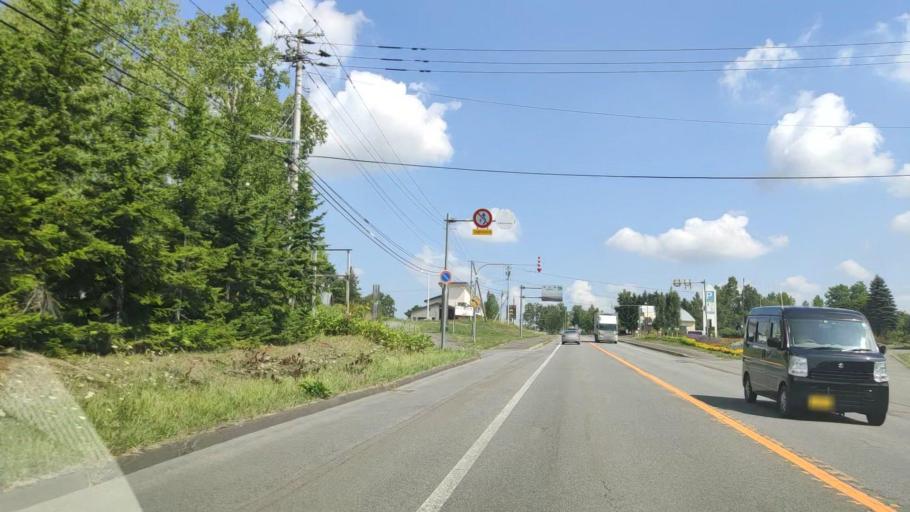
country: JP
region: Hokkaido
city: Shimo-furano
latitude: 43.5169
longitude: 142.4475
